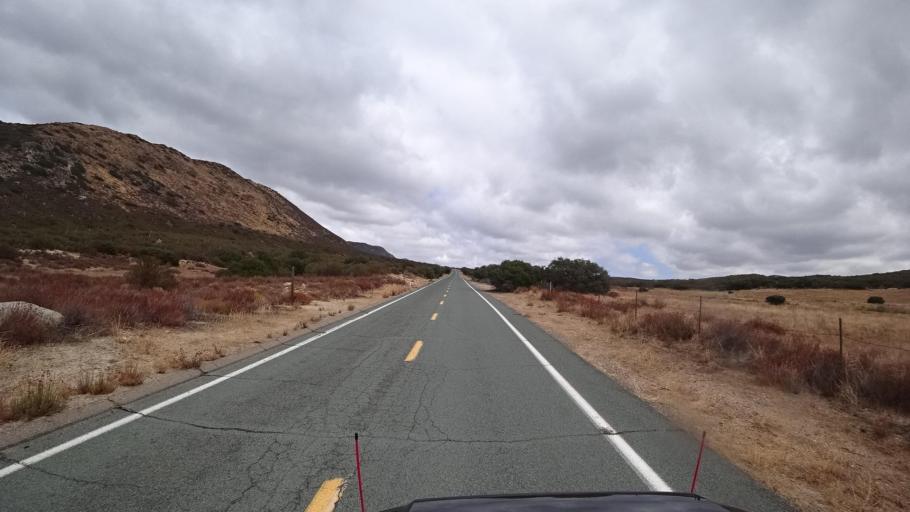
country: US
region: California
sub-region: San Diego County
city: Pine Valley
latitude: 32.7289
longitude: -116.4597
